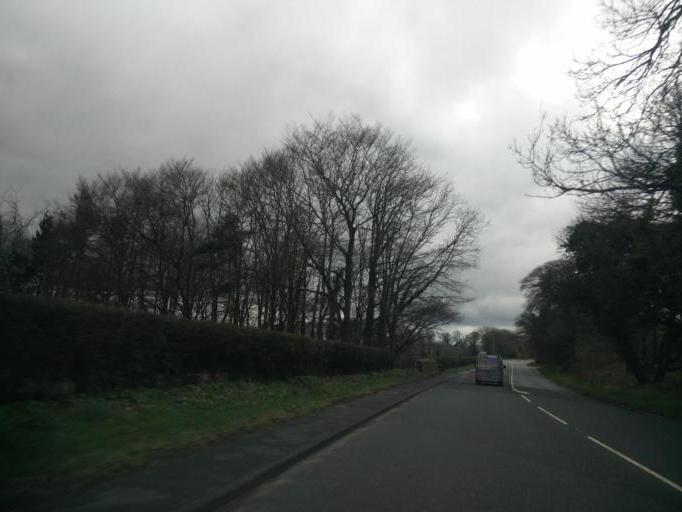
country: GB
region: England
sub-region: County Durham
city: Ushaw Moor
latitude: 54.7442
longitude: -1.6356
